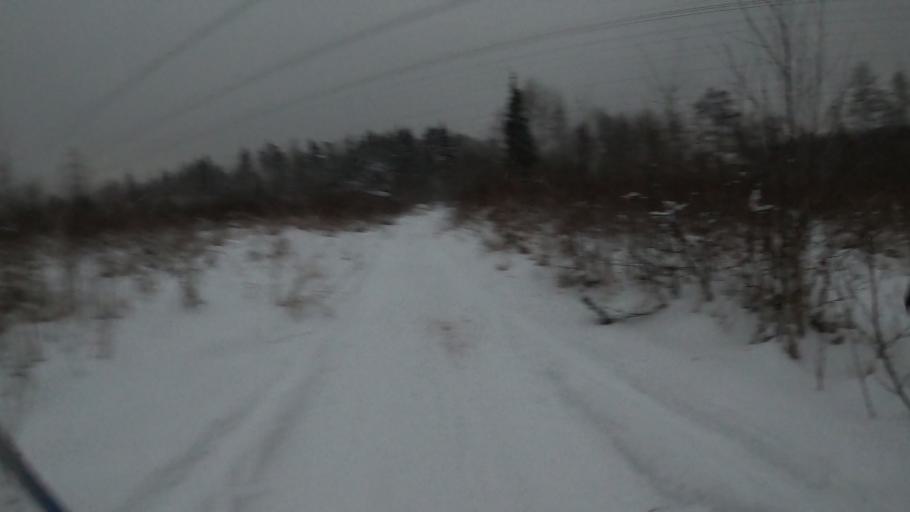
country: RU
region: Moskovskaya
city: Nakhabino
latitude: 55.8900
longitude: 37.2124
